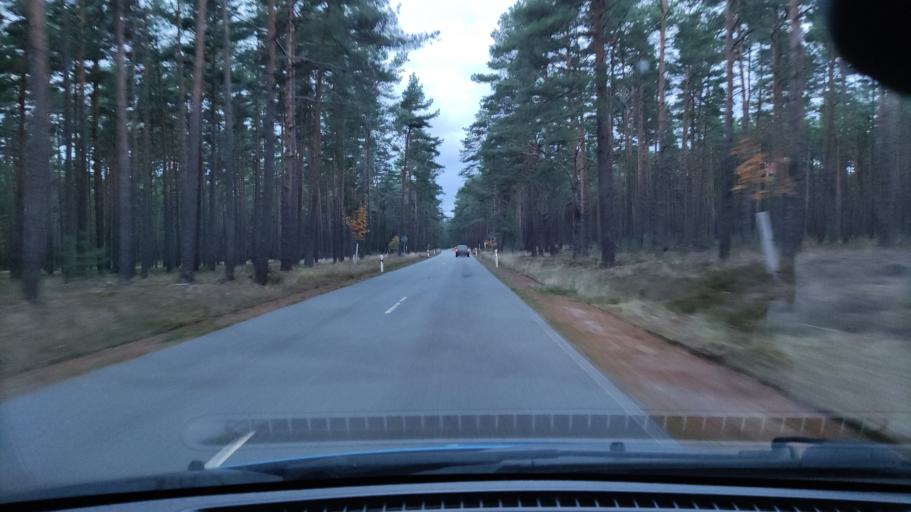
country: DE
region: Lower Saxony
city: Gorleben
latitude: 53.0137
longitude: 11.3888
